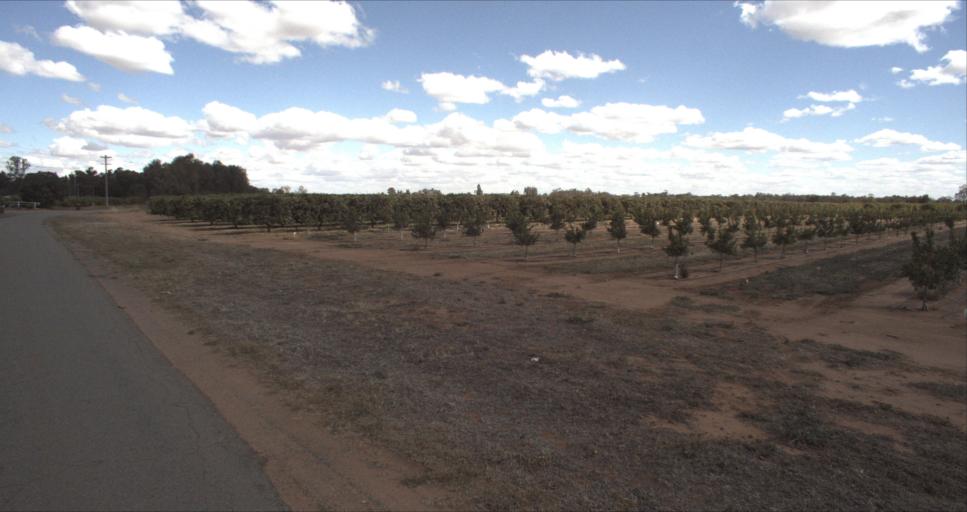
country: AU
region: New South Wales
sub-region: Leeton
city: Leeton
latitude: -34.5101
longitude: 146.2318
